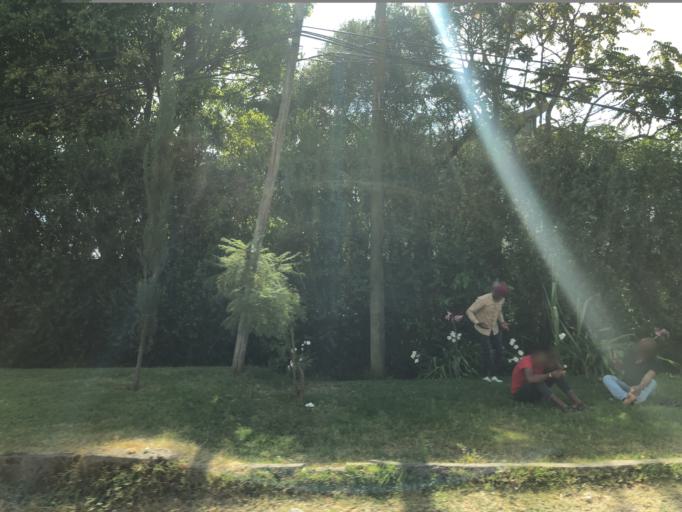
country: ET
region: Adis Abeba
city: Addis Ababa
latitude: 8.9950
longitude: 38.7800
